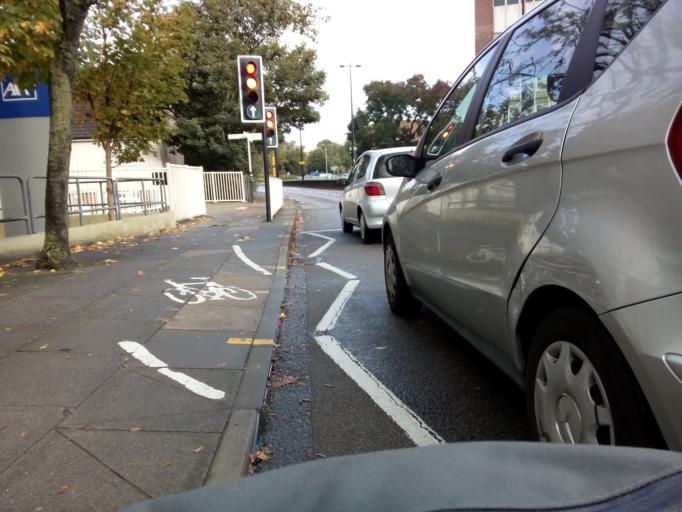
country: GB
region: England
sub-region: Suffolk
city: Ipswich
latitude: 52.0568
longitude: 1.1482
